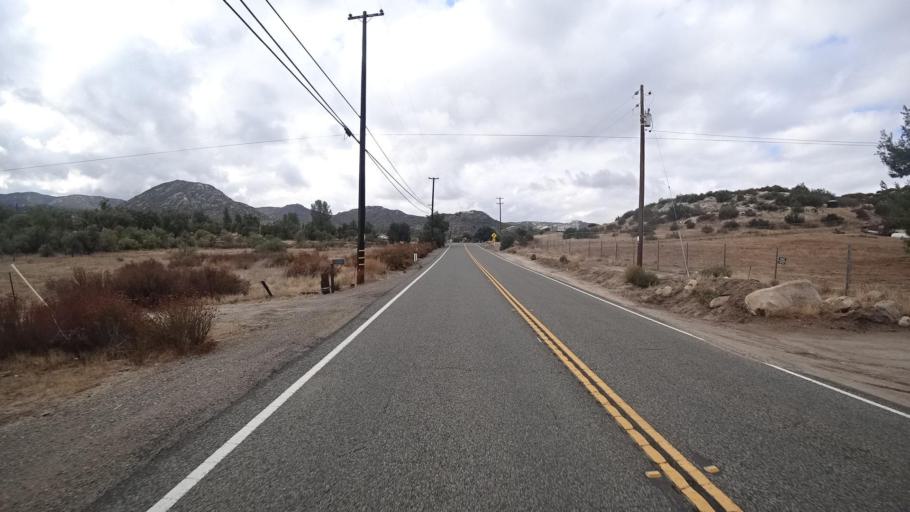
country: US
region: California
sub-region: San Diego County
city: Campo
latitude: 32.6334
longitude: -116.4331
